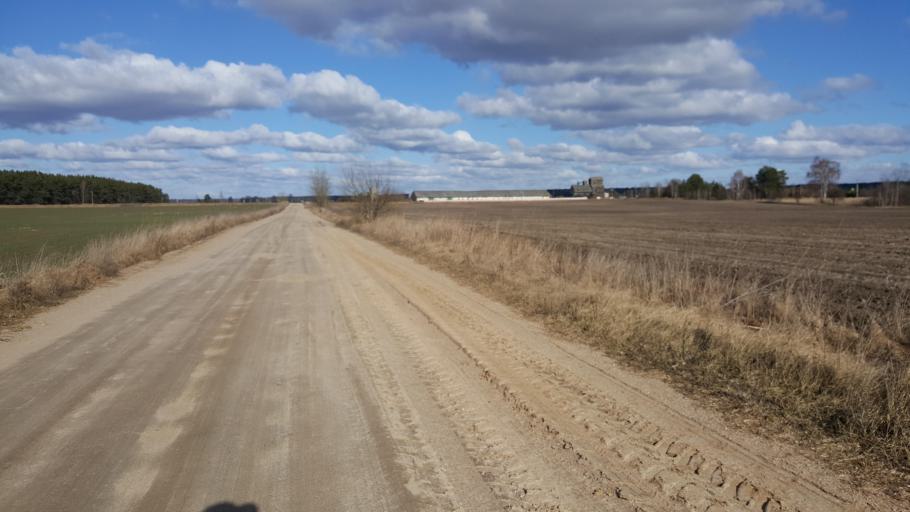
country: BY
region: Brest
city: Kamyanyets
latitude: 52.3919
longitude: 23.8797
